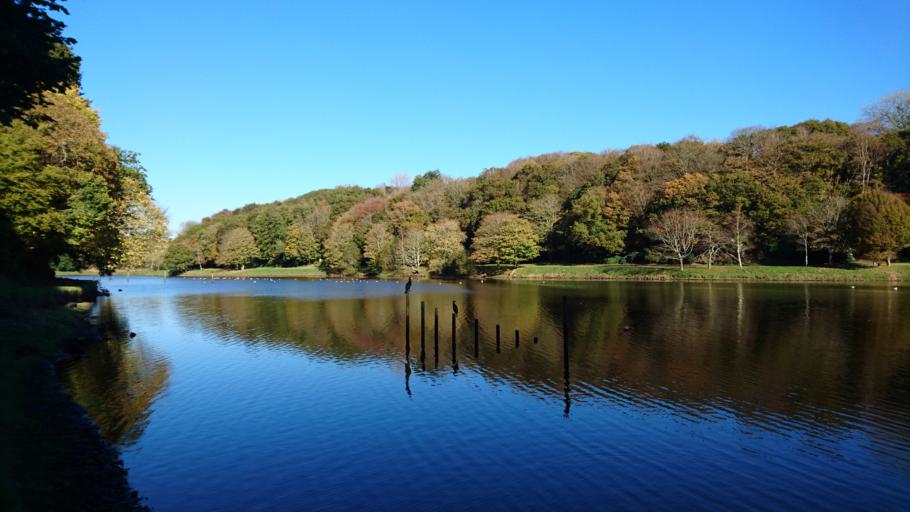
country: FR
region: Brittany
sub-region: Departement du Finistere
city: Bohars
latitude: 48.4062
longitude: -4.5246
